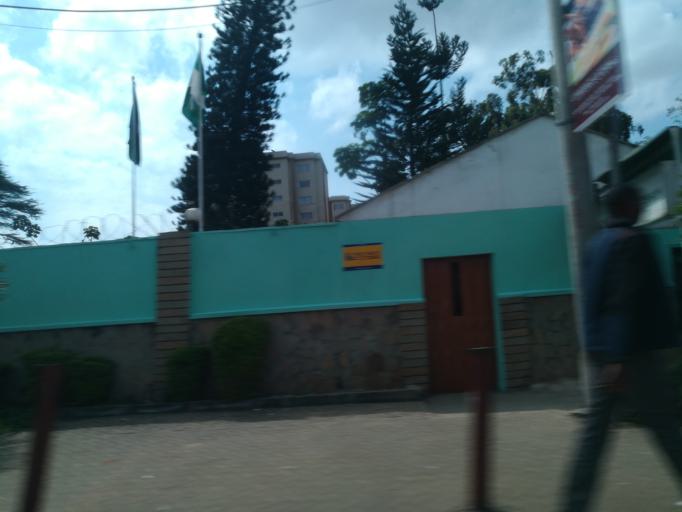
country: KE
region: Nairobi Area
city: Nairobi
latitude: -1.2890
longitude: 36.7893
